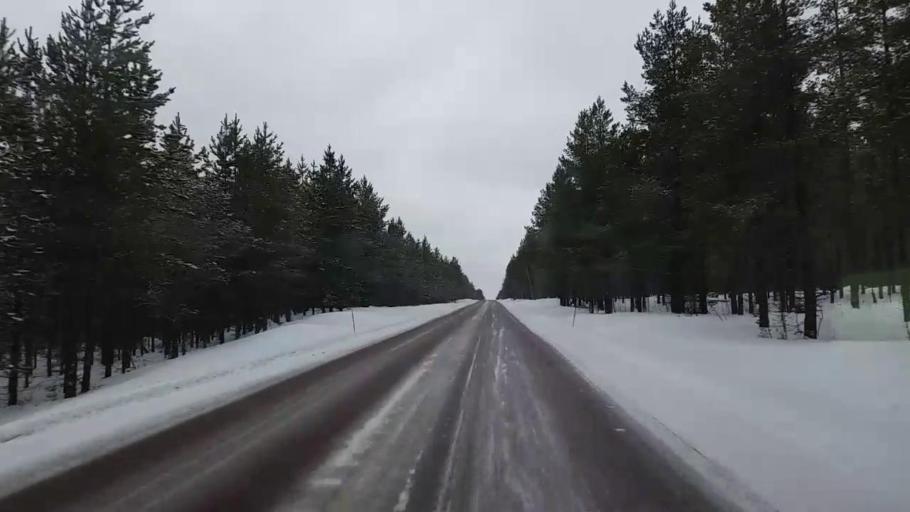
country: SE
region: Jaemtland
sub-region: Bergs Kommun
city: Hoverberg
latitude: 62.4420
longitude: 14.5769
